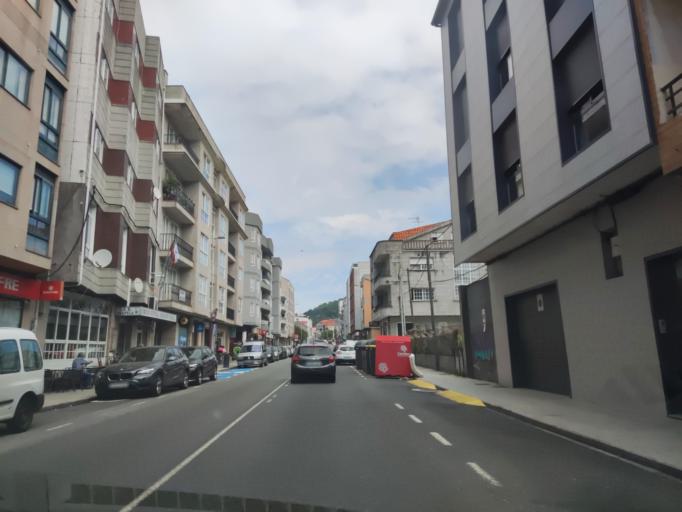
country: ES
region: Galicia
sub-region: Provincia de Pontevedra
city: Vigo
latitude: 42.2665
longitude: -8.6726
